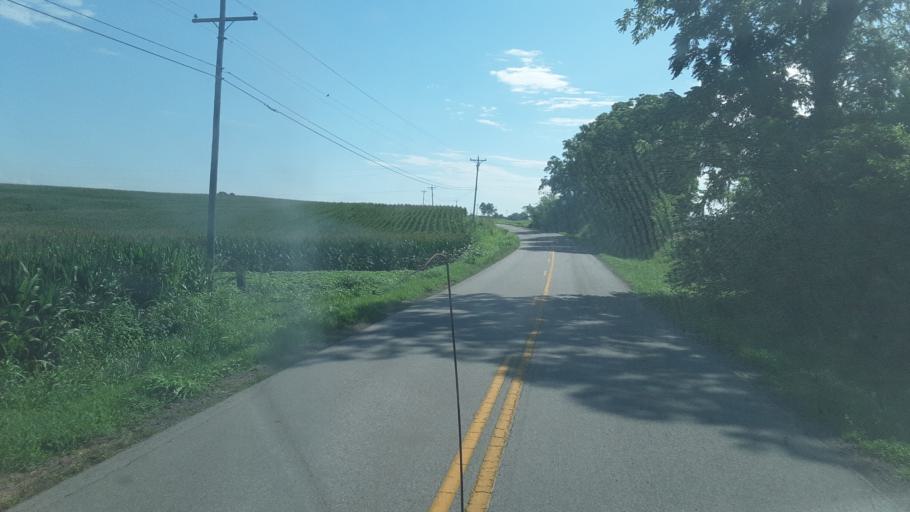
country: US
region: Kentucky
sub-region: Todd County
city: Guthrie
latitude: 36.7350
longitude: -87.2540
